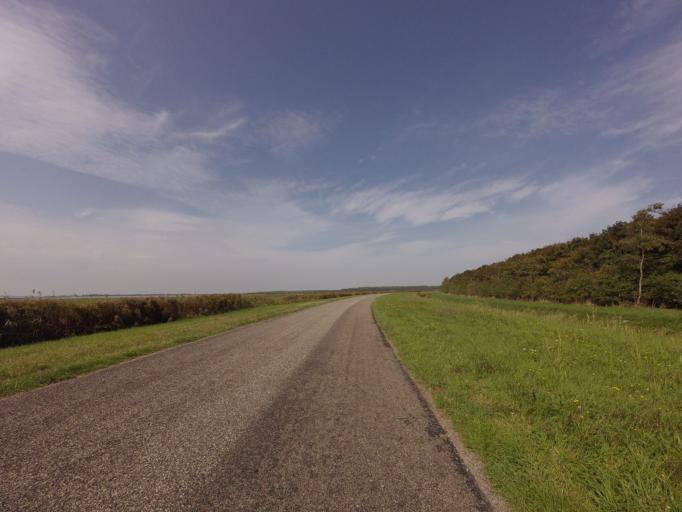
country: NL
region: Groningen
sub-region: Gemeente De Marne
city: Ulrum
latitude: 53.3572
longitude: 6.2625
